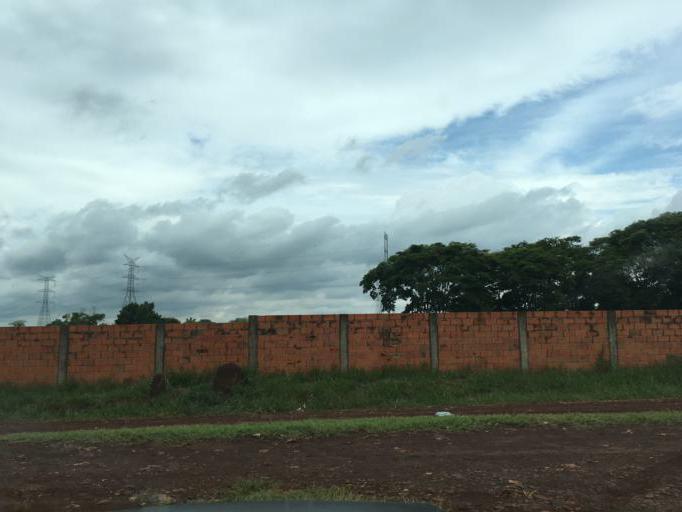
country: PY
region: Alto Parana
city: Ciudad del Este
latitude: -25.4249
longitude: -54.6447
